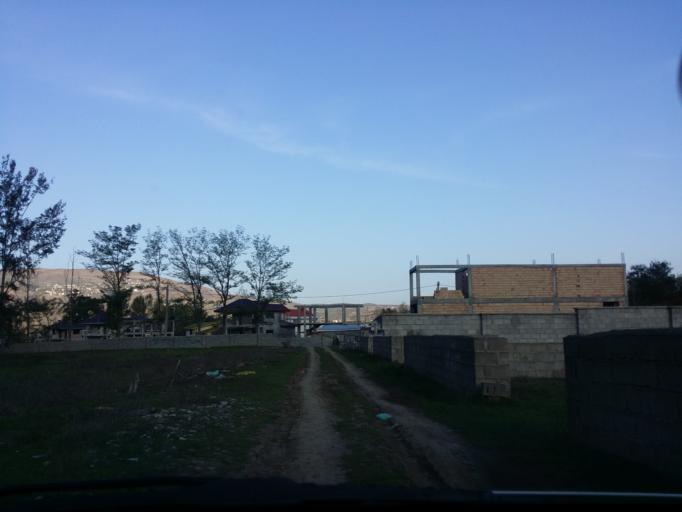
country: IR
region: Mazandaran
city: `Abbasabad
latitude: 36.5138
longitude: 51.1806
